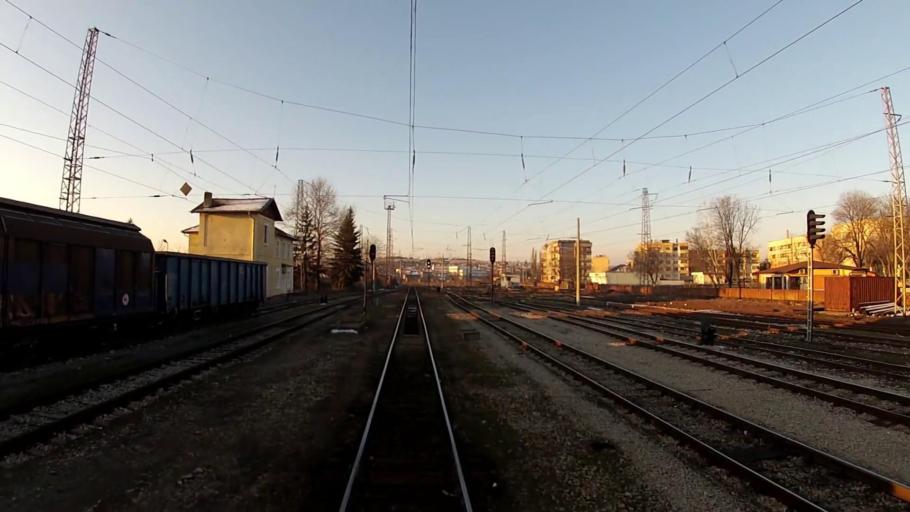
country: BG
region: Sofiya
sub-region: Obshtina Dragoman
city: Dragoman
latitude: 42.9190
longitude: 22.9295
